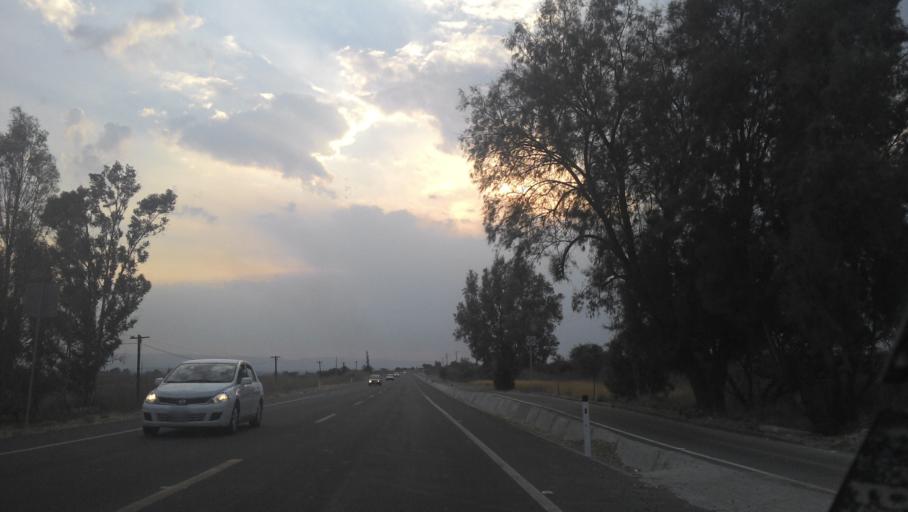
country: MX
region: Guanajuato
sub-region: San Francisco del Rincon
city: San Ignacio de Hidalgo
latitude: 20.8945
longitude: -101.9281
